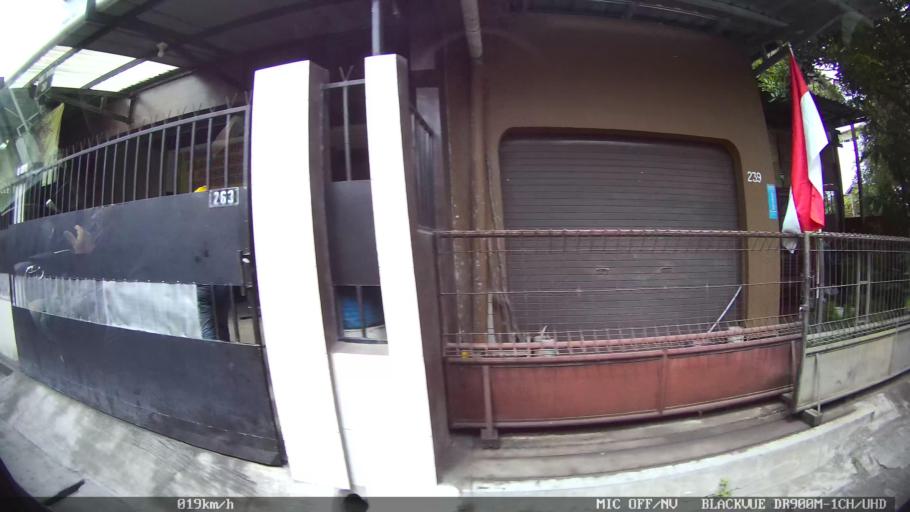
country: ID
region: Daerah Istimewa Yogyakarta
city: Gamping Lor
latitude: -7.8057
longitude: 110.3374
